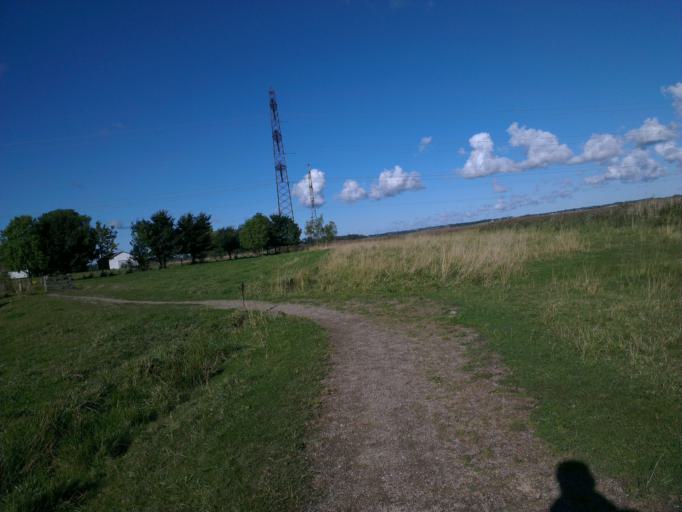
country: DK
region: Capital Region
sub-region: Frederikssund Kommune
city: Frederikssund
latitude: 55.7946
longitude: 12.0424
